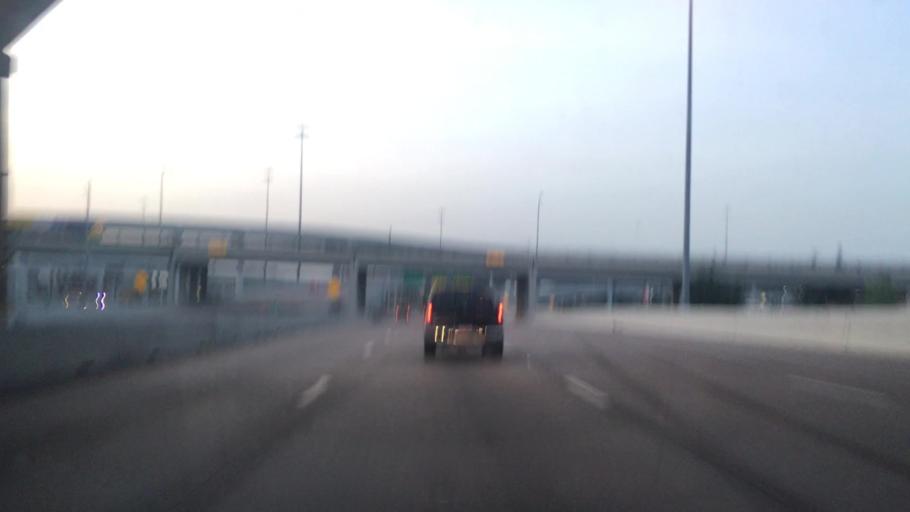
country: US
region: Texas
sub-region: Dallas County
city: Dallas
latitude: 32.7697
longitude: -96.8091
